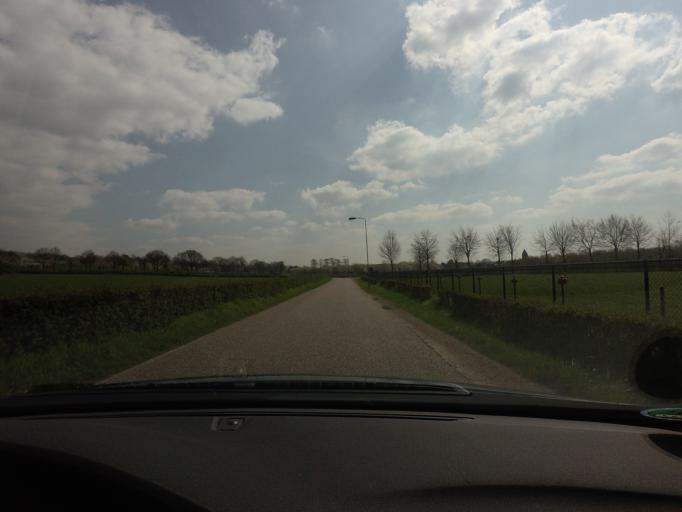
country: NL
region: Limburg
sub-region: Eijsden-Margraten
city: Eijsden
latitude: 50.7669
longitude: 5.7261
